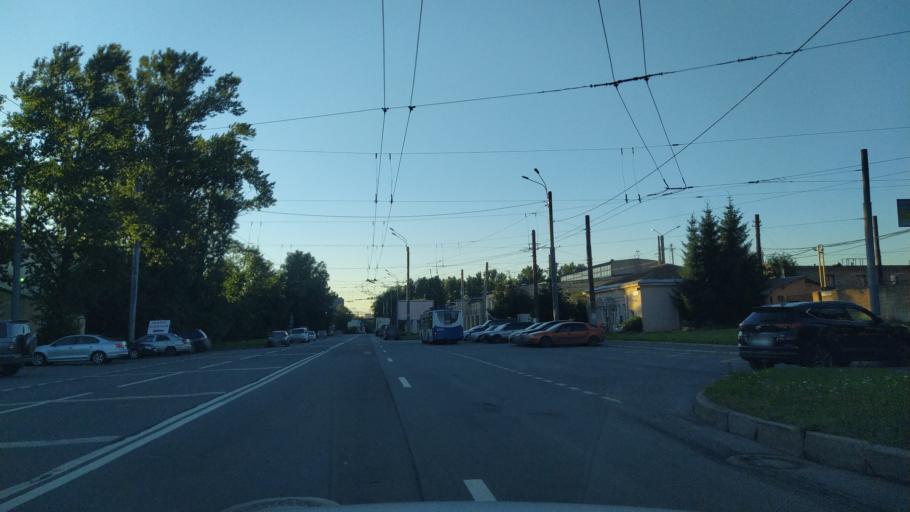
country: RU
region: Leningrad
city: Finlyandskiy
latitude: 59.9680
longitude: 30.3662
